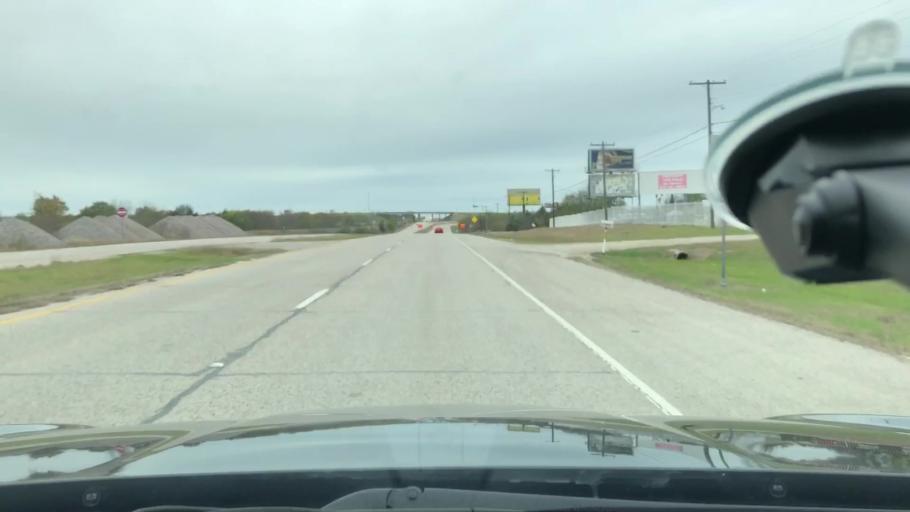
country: US
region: Texas
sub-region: Kaufman County
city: Talty
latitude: 32.7384
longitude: -96.3467
